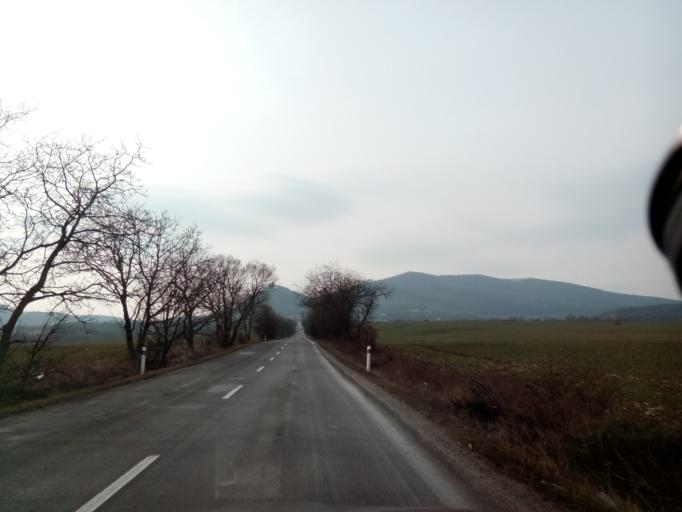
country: SK
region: Kosicky
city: Secovce
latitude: 48.6350
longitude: 21.5022
